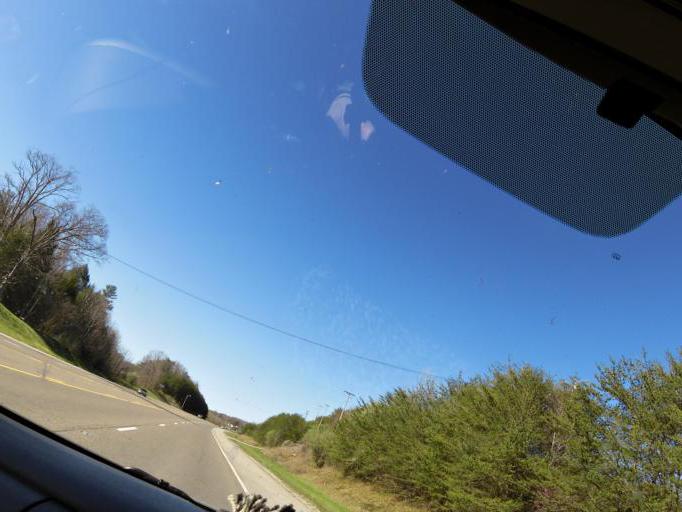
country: US
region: Tennessee
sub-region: Scott County
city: Huntsville
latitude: 36.4345
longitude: -84.5389
